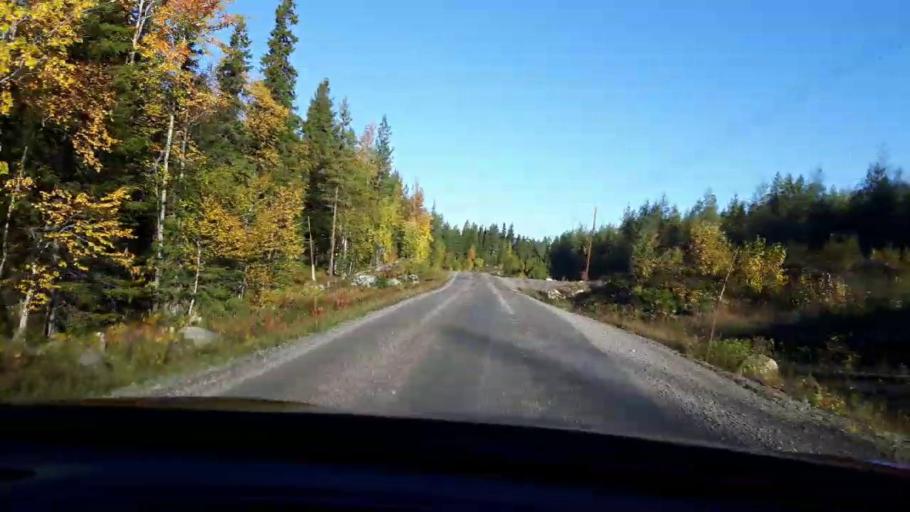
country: SE
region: Jaemtland
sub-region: Stroemsunds Kommun
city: Stroemsund
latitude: 64.3672
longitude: 15.1629
